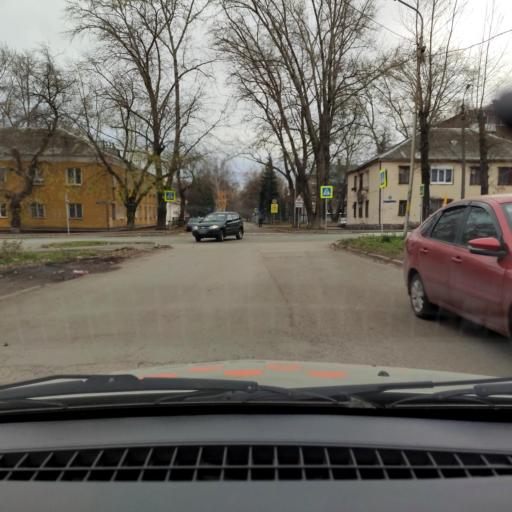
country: RU
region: Bashkortostan
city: Ufa
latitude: 54.8158
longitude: 56.1206
